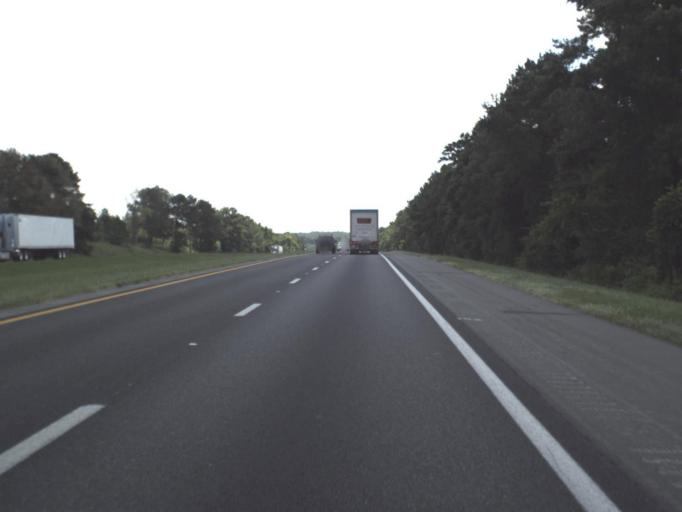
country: US
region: Florida
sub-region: Madison County
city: Madison
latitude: 30.4354
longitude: -83.4933
